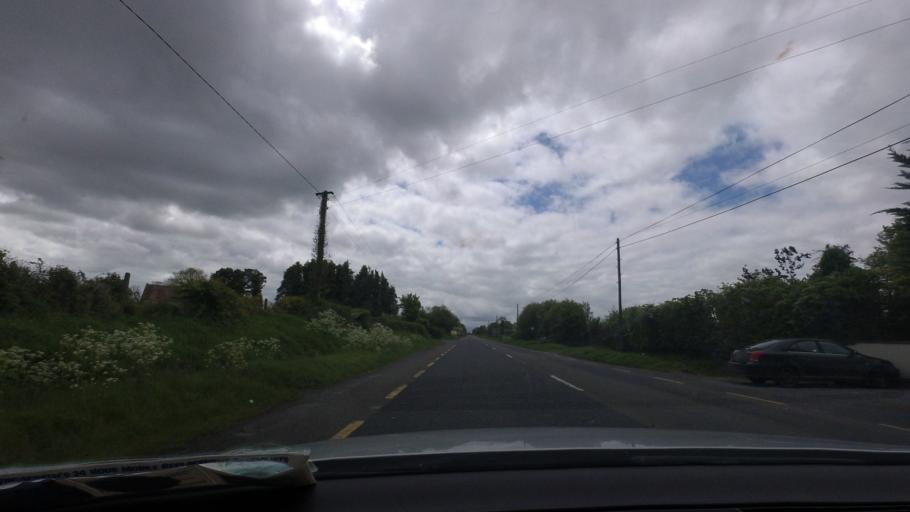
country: IE
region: Munster
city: Thurles
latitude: 52.5969
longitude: -7.8023
